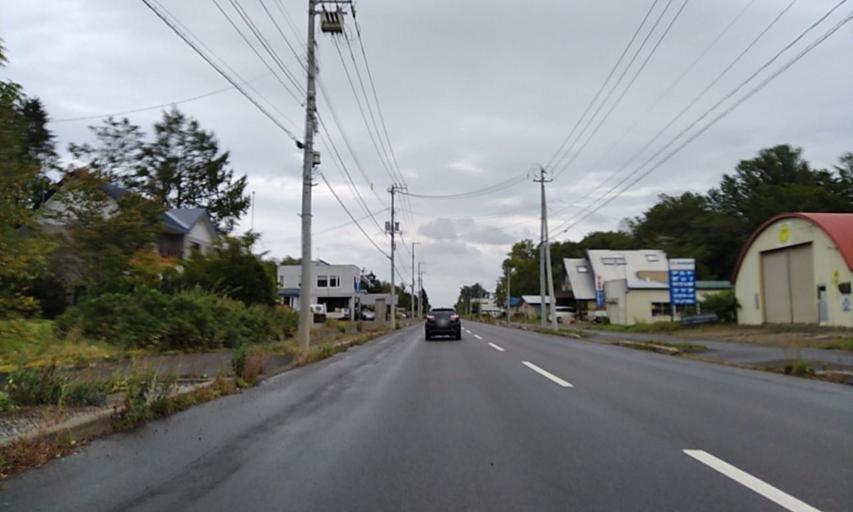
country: JP
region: Hokkaido
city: Kitami
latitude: 44.0818
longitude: 143.9452
